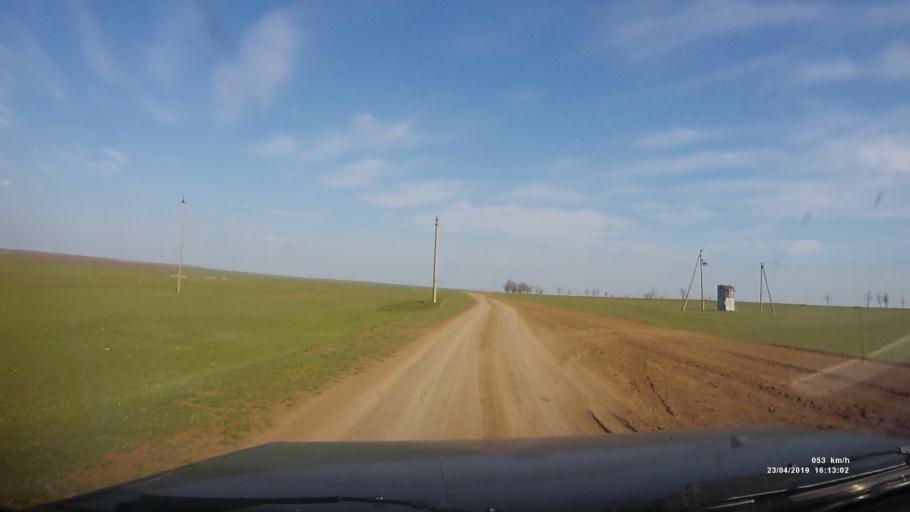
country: RU
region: Kalmykiya
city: Priyutnoye
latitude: 46.4644
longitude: 43.1324
